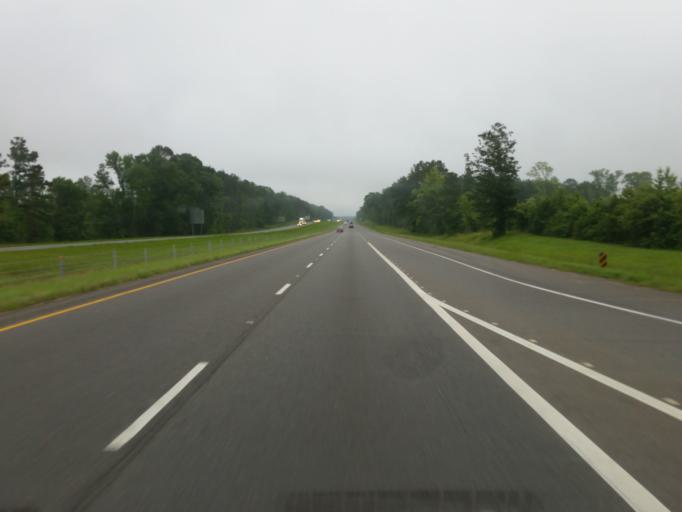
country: US
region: Louisiana
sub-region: Bossier Parish
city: Haughton
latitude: 32.5519
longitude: -93.5114
